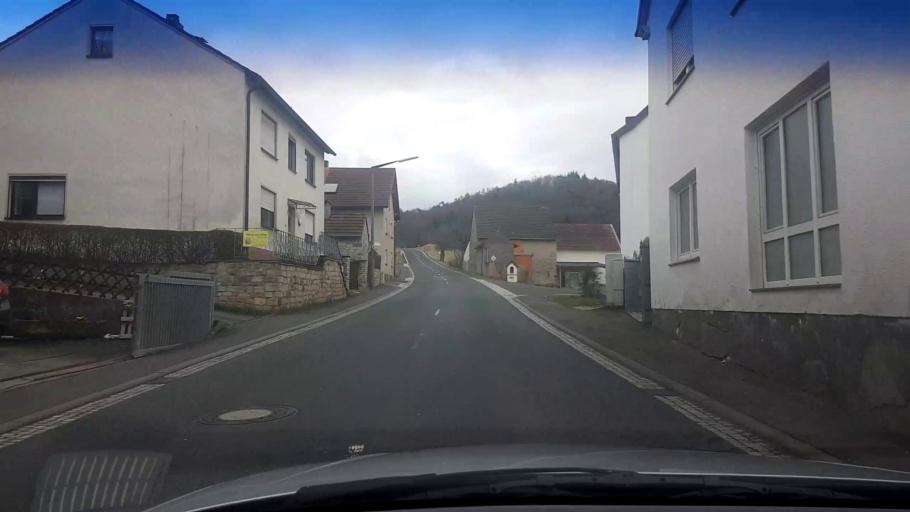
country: DE
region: Bavaria
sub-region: Regierungsbezirk Unterfranken
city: Knetzgau
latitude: 49.9626
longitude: 10.5653
